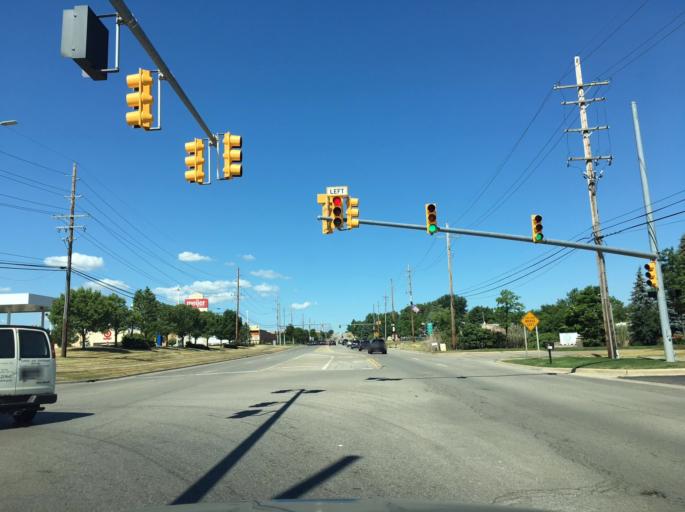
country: US
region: Michigan
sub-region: Oakland County
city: Auburn Hills
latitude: 42.7077
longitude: -83.2876
